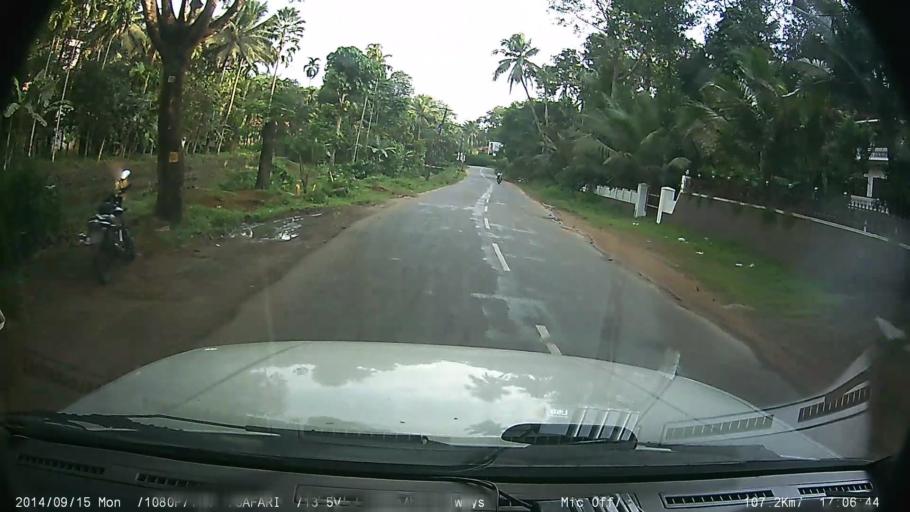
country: IN
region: Kerala
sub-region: Kottayam
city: Palackattumala
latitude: 9.8001
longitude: 76.5743
